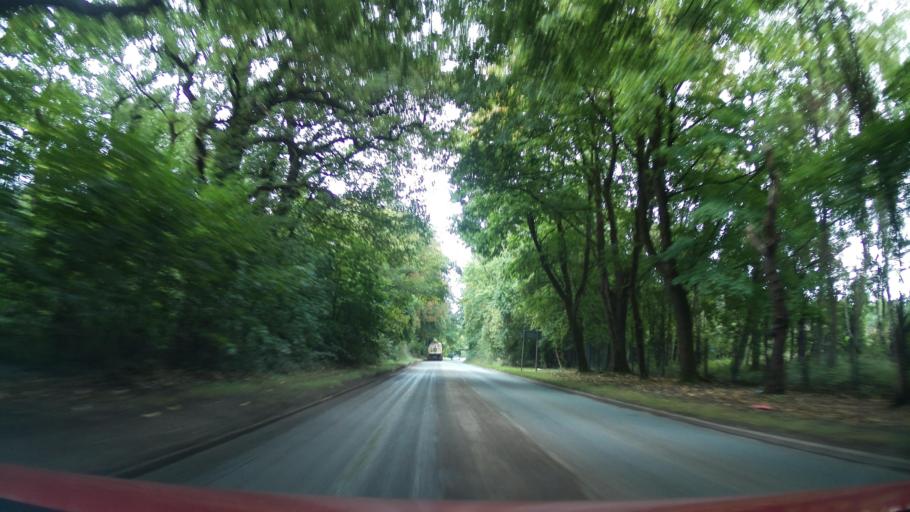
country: GB
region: England
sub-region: Staffordshire
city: Eccleshall
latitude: 52.9016
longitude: -2.2159
